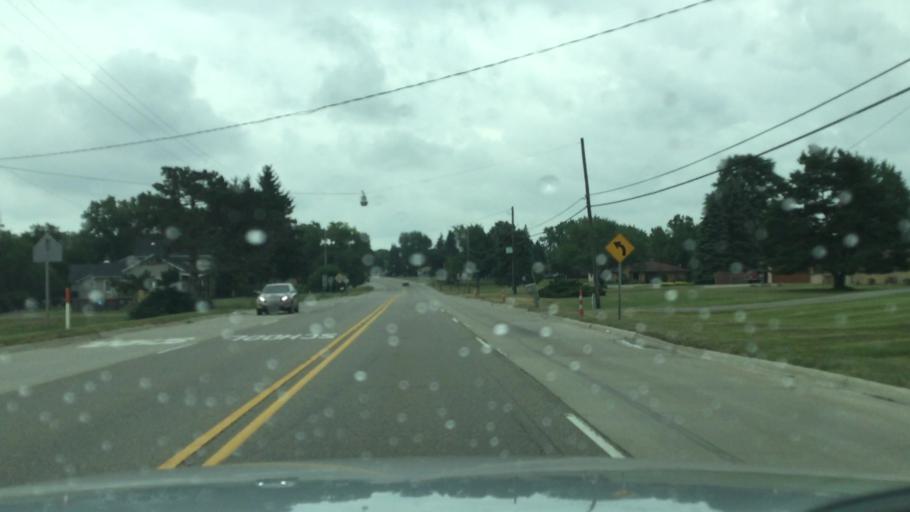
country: US
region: Michigan
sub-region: Genesee County
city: Flint
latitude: 43.0241
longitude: -83.7566
